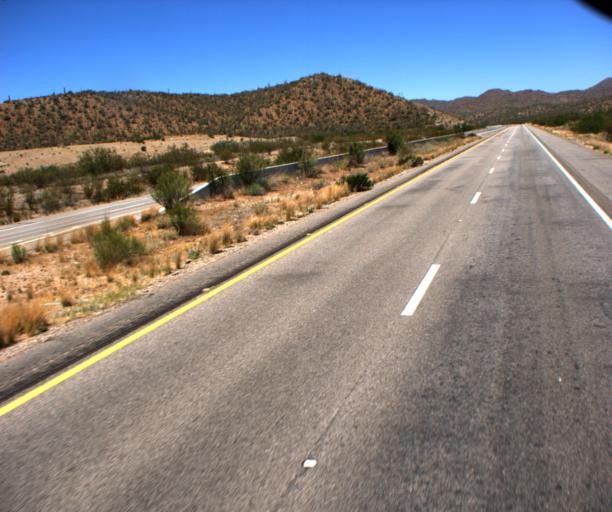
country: US
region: Arizona
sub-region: Yavapai County
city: Bagdad
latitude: 34.3735
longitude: -113.1894
